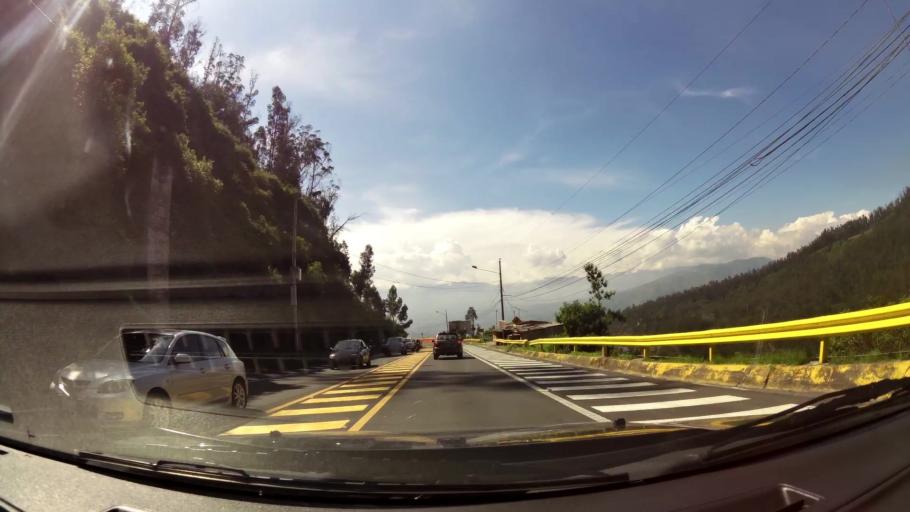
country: EC
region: Pichincha
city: Quito
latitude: -0.1937
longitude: -78.4663
